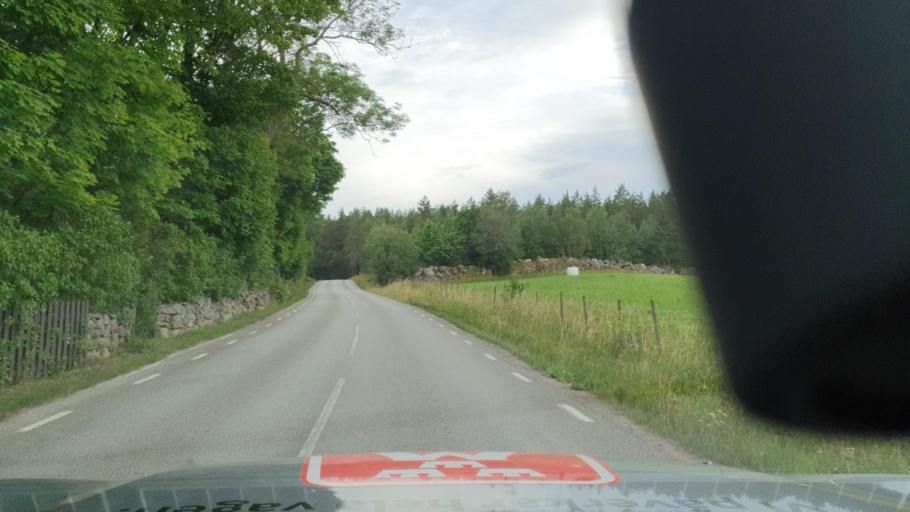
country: SE
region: Kalmar
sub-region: Kalmar Kommun
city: Trekanten
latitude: 56.6508
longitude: 16.0115
